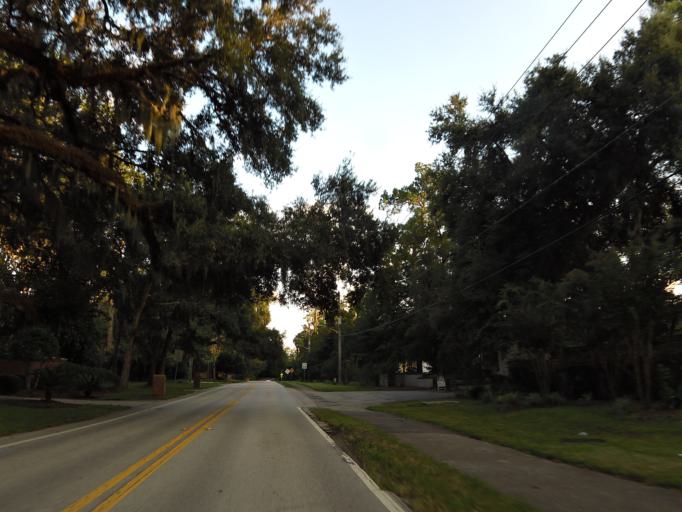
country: US
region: Florida
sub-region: Clay County
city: Orange Park
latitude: 30.1974
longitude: -81.6324
